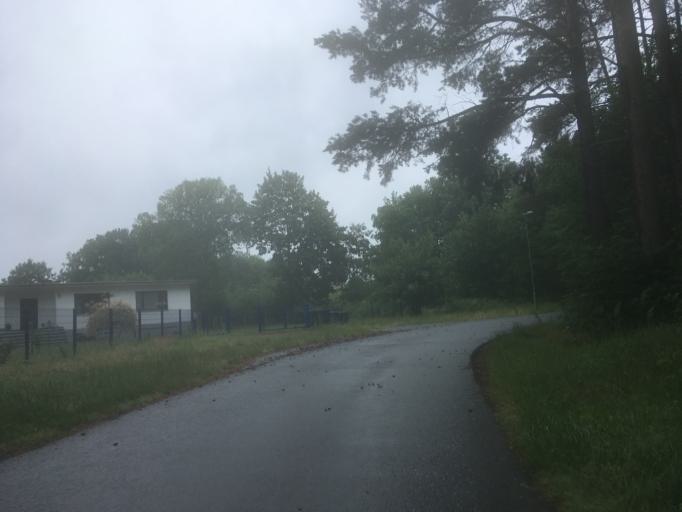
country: DE
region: Brandenburg
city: Liebenwalde
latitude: 52.8900
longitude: 13.3810
